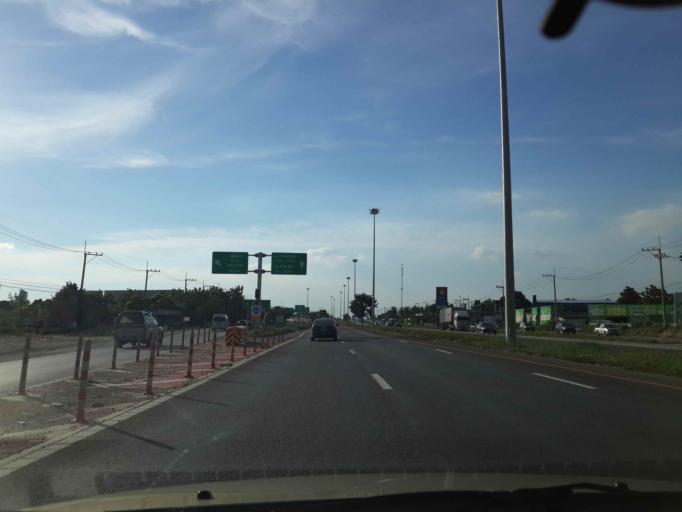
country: TH
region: Chon Buri
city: Phatthaya
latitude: 12.9582
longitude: 100.9848
